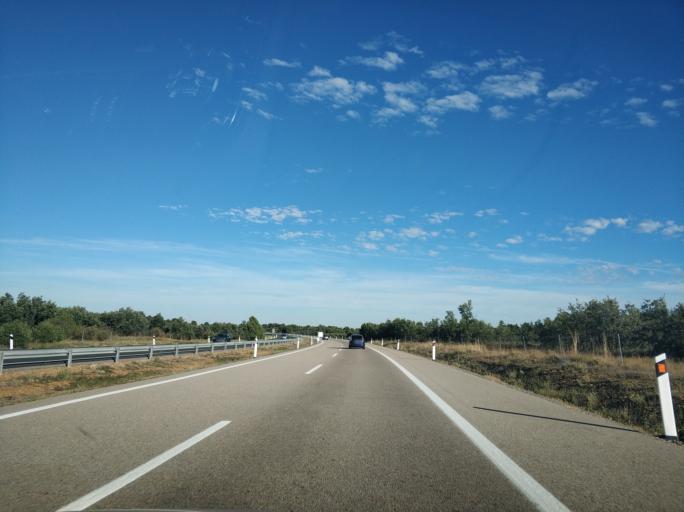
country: ES
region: Castille and Leon
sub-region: Provincia de Leon
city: Valverde de la Virgen
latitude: 42.6095
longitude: -5.7280
